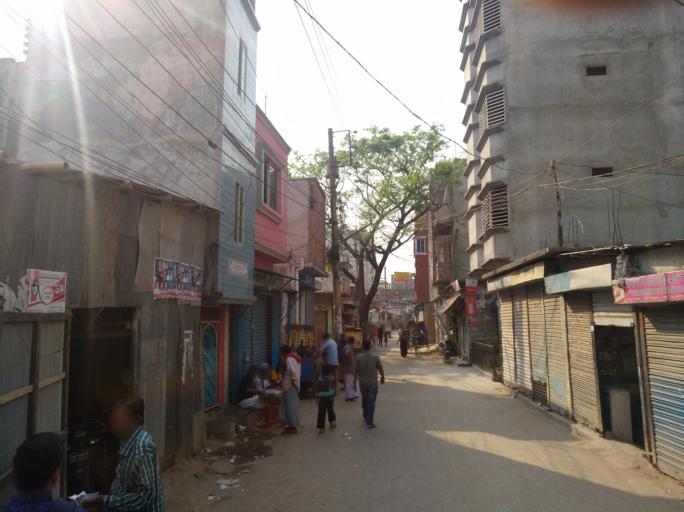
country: BD
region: Dhaka
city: Azimpur
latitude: 23.7147
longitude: 90.3744
